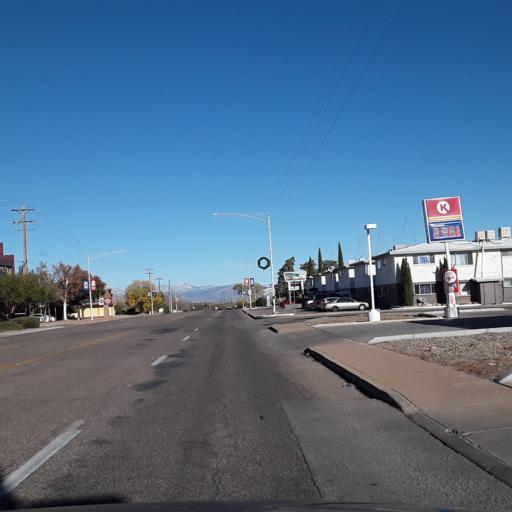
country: US
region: Arizona
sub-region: Cochise County
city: Sierra Vista
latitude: 31.5552
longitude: -110.3058
